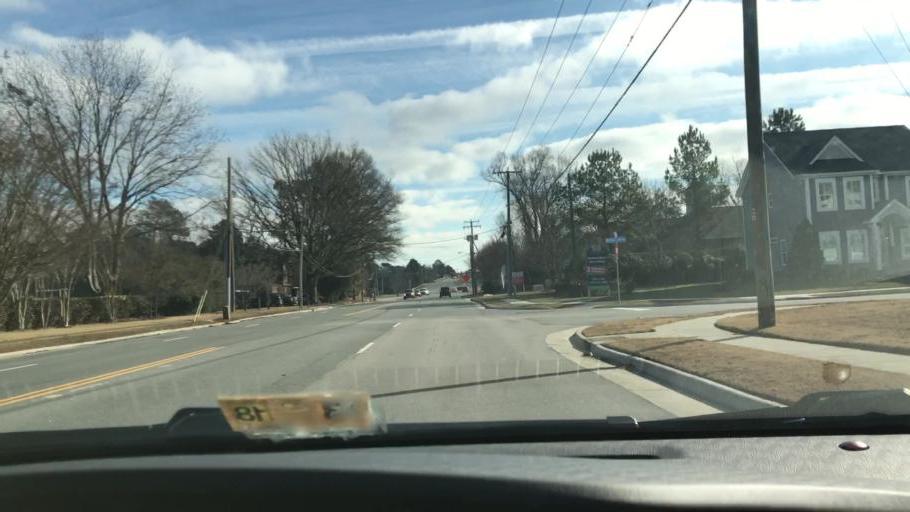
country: US
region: Virginia
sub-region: City of Chesapeake
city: Chesapeake
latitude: 36.6896
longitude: -76.2340
